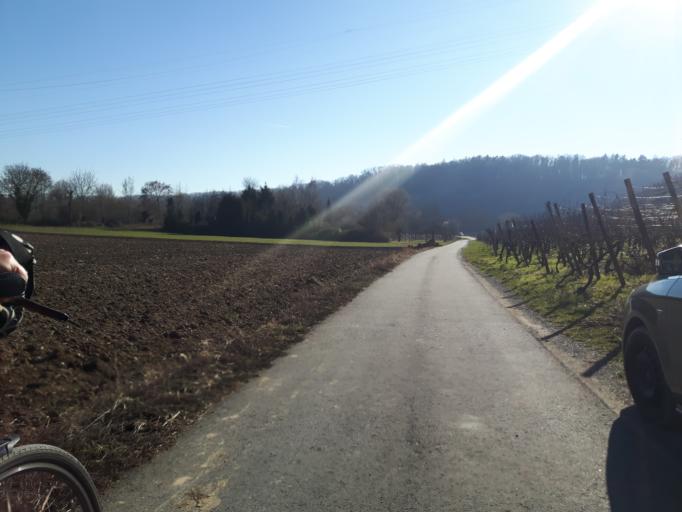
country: DE
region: Baden-Wuerttemberg
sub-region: Regierungsbezirk Stuttgart
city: Lauffen am Neckar
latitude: 49.0693
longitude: 9.1286
